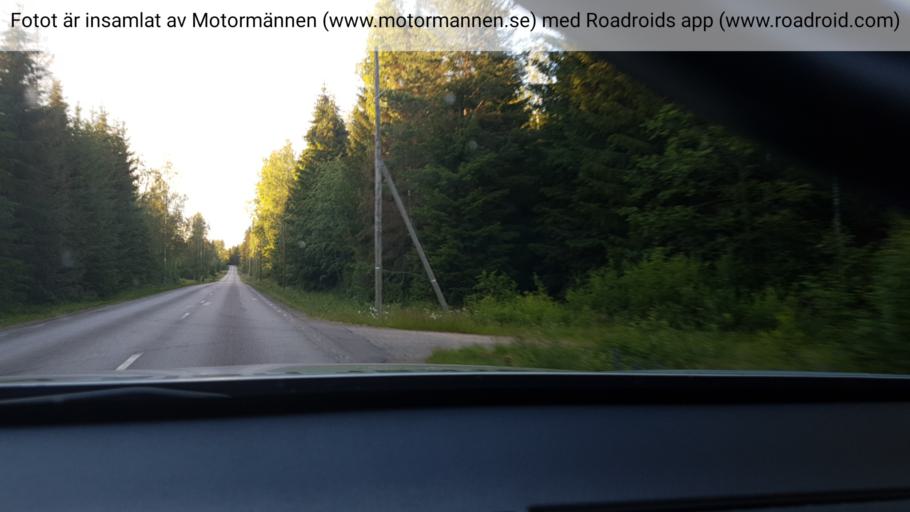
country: SE
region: Vaermland
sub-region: Torsby Kommun
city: Torsby
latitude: 60.0882
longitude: 13.0886
